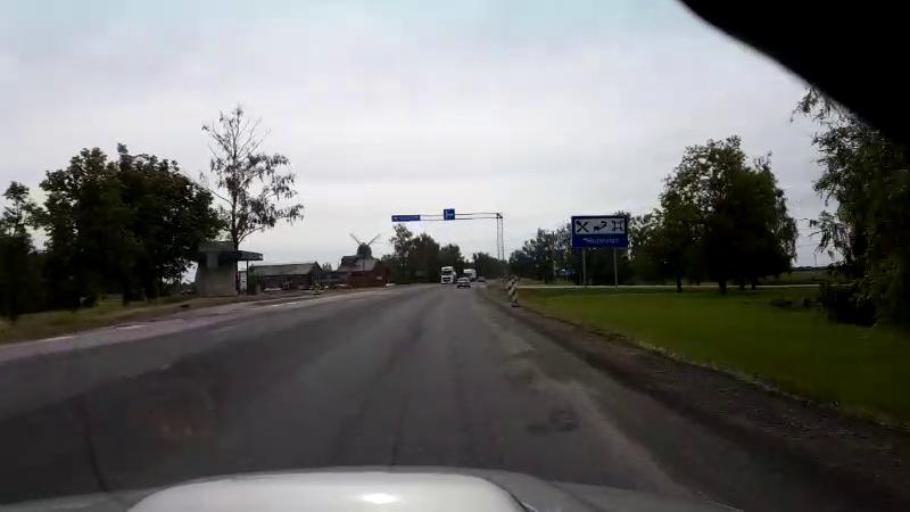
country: LV
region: Bauskas Rajons
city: Bauska
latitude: 56.3598
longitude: 24.2831
